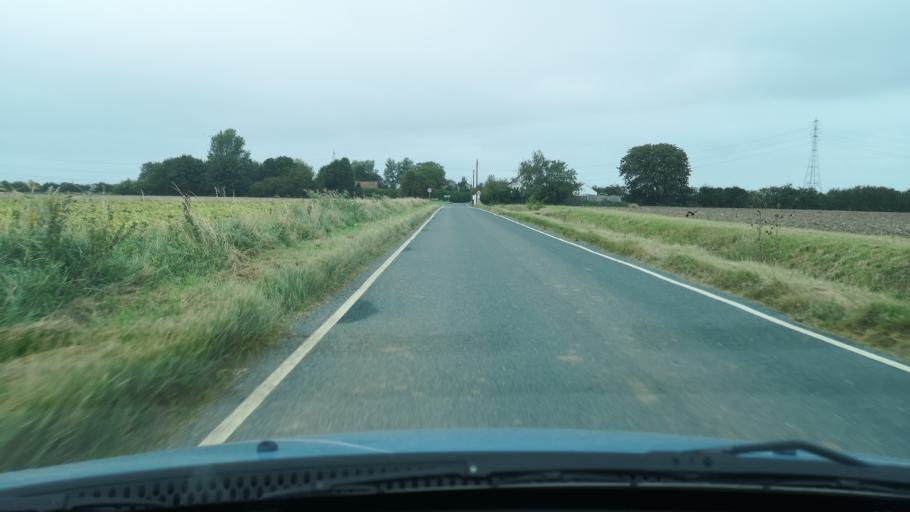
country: GB
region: England
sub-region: North Lincolnshire
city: Burton upon Stather
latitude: 53.6977
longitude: -0.7333
